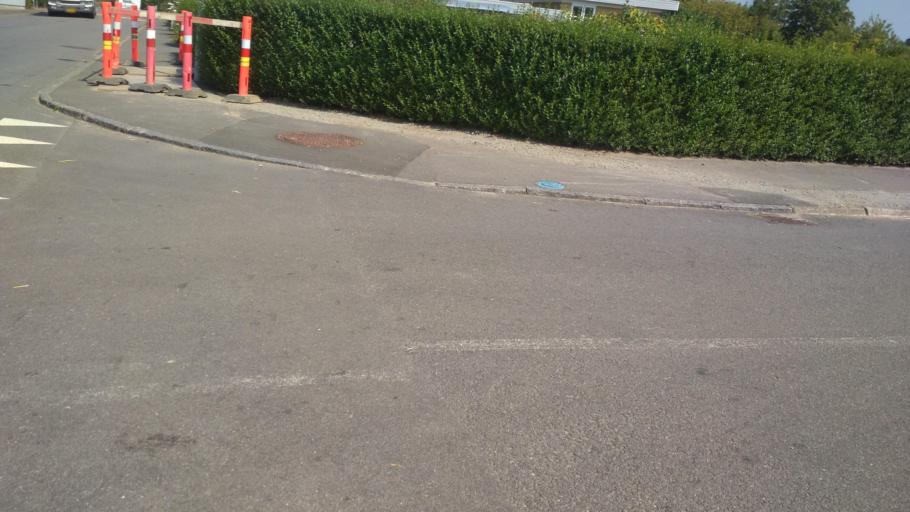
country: DK
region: Capital Region
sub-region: Bornholm Kommune
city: Akirkeby
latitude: 55.0683
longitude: 14.9265
